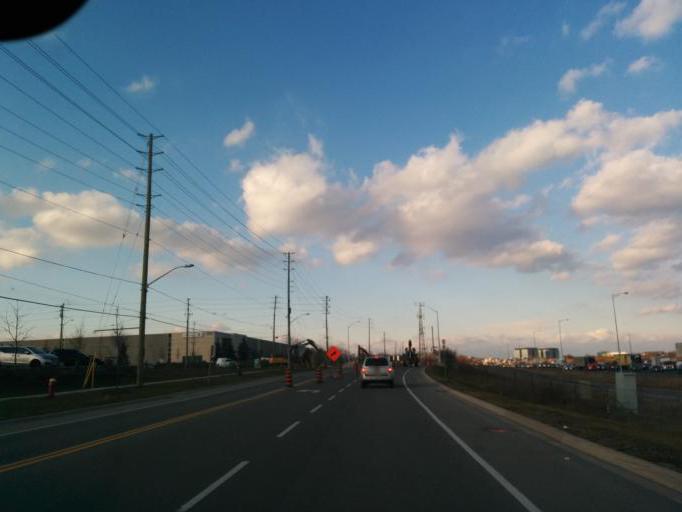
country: CA
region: Ontario
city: Oakville
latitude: 43.4877
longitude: -79.6740
